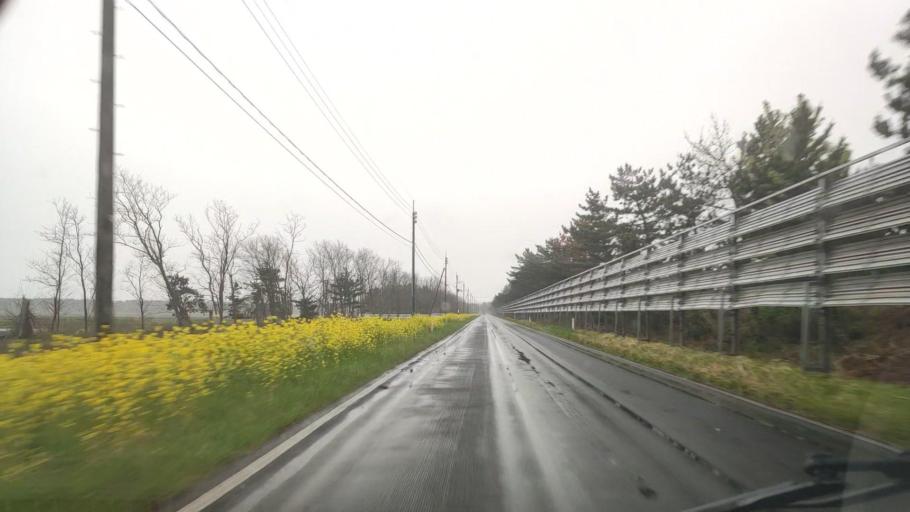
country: JP
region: Akita
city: Tenno
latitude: 40.0427
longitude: 139.9566
